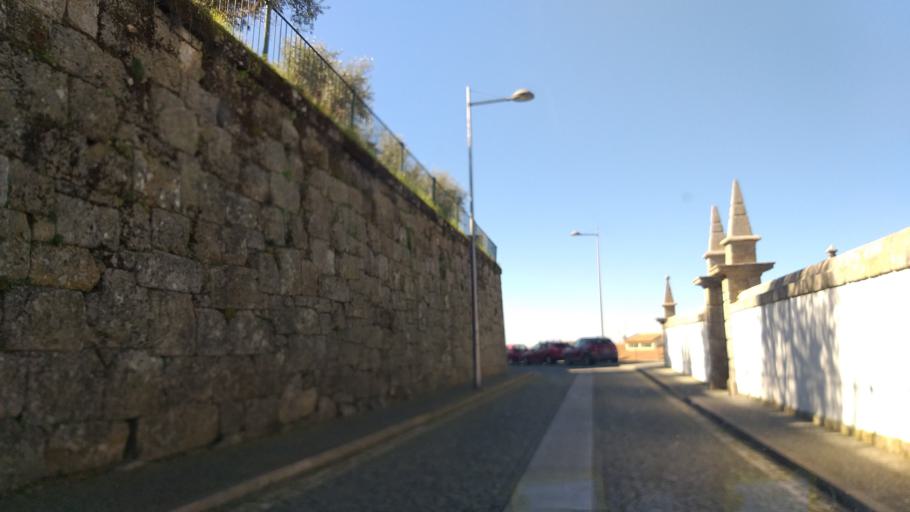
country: PT
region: Guarda
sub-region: Manteigas
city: Manteigas
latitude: 40.4967
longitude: -7.5908
